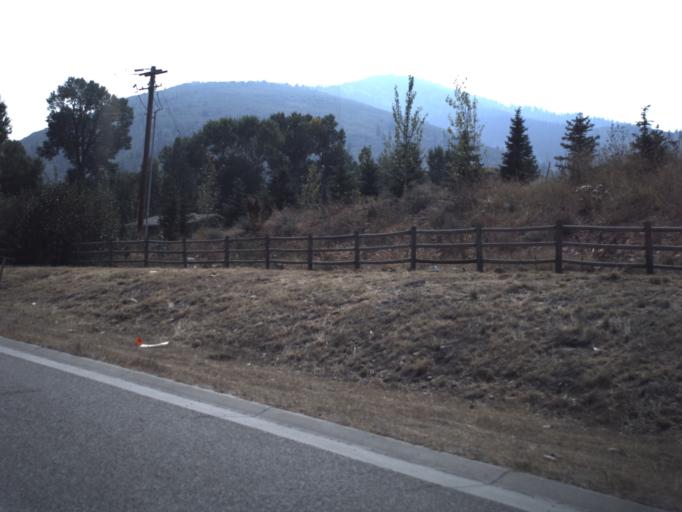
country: US
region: Utah
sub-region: Summit County
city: Snyderville
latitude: 40.6863
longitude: -111.5433
